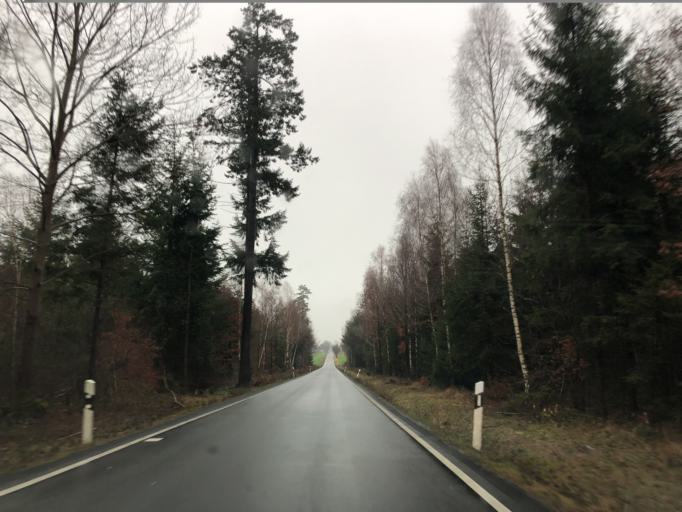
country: DE
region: Hesse
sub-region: Regierungsbezirk Darmstadt
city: Lutzelbach
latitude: 49.7262
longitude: 9.0852
